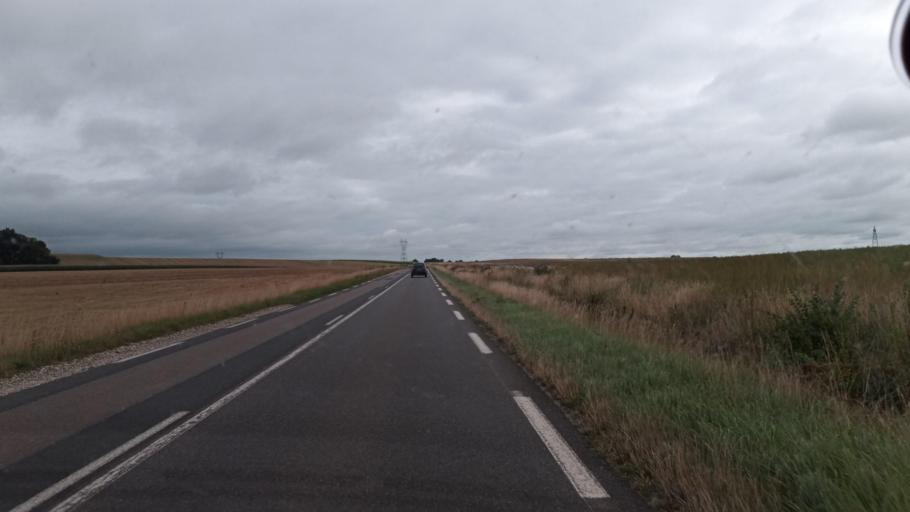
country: FR
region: Ile-de-France
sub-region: Departement de Seine-et-Marne
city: Voulx
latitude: 48.3235
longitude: 2.9530
